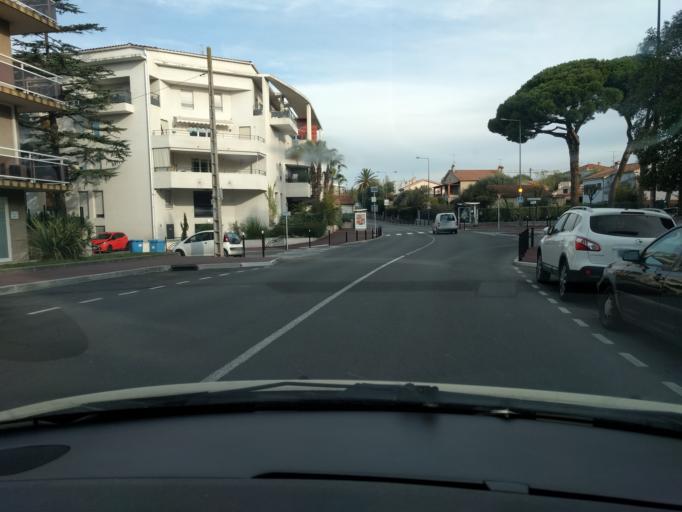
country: FR
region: Provence-Alpes-Cote d'Azur
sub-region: Departement des Alpes-Maritimes
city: Mandelieu-la-Napoule
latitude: 43.5559
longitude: 6.9700
